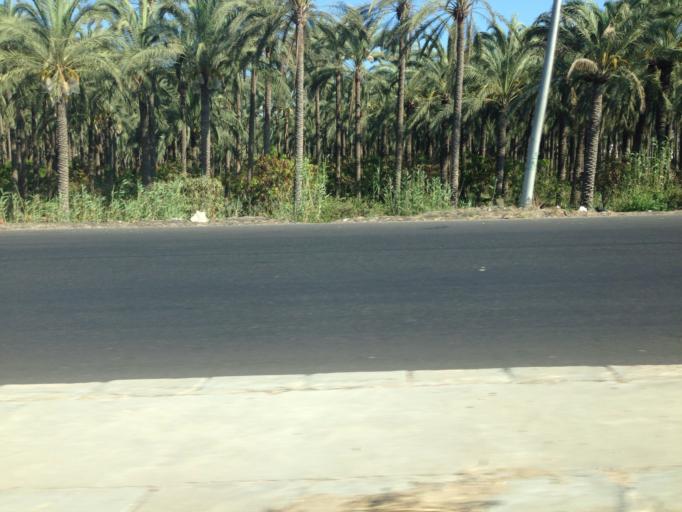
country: EG
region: Al Buhayrah
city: Idku
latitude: 31.2873
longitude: 30.2438
